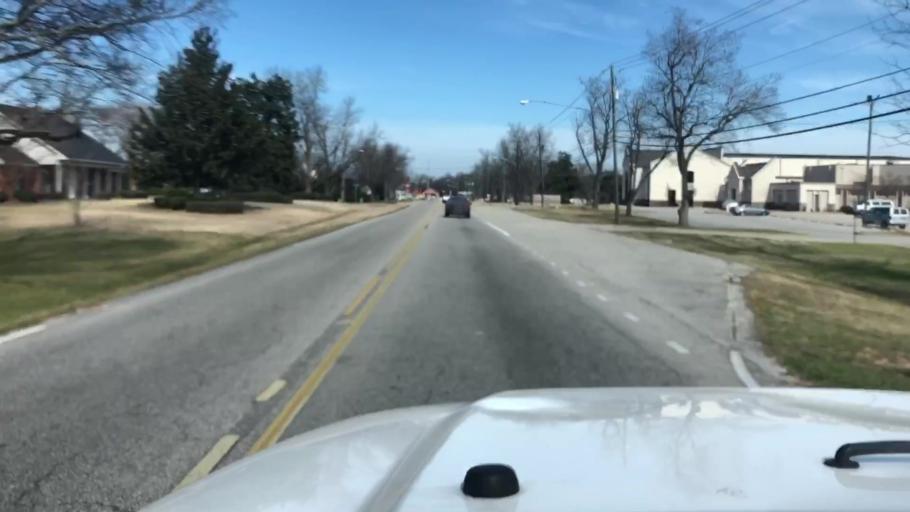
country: US
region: Alabama
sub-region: Montgomery County
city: Montgomery
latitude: 32.3774
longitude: -86.1914
